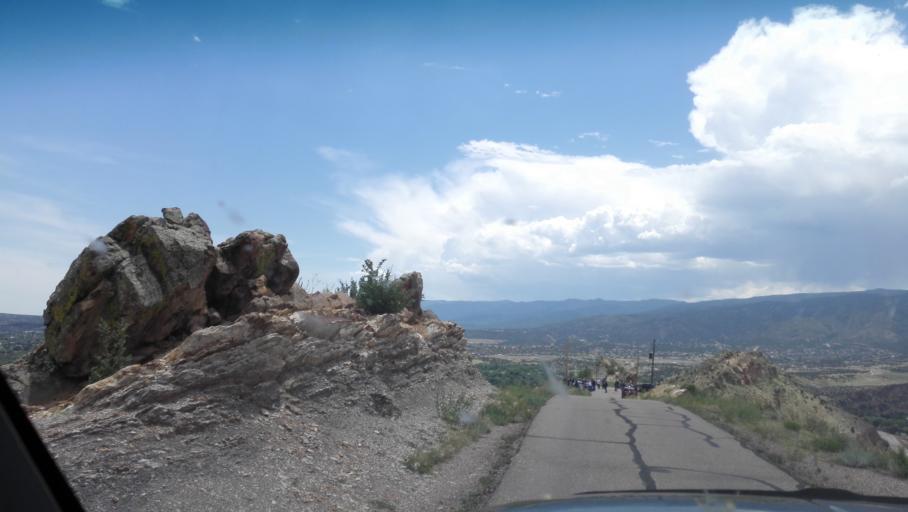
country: US
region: Colorado
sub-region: Fremont County
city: Canon City
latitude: 38.4511
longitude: -105.2493
